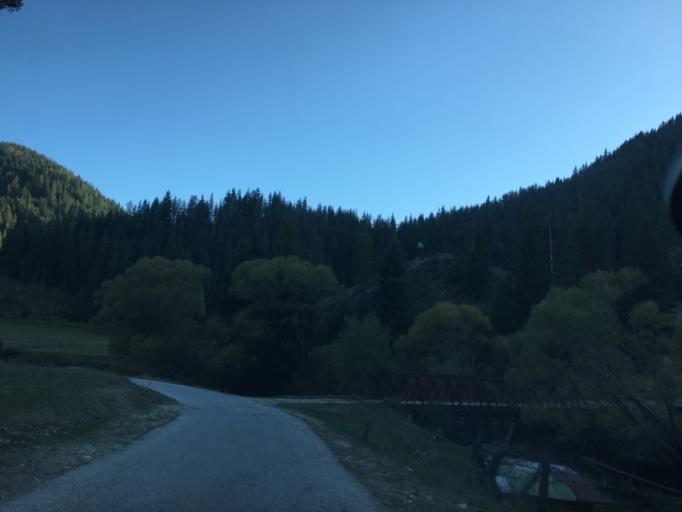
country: BG
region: Smolyan
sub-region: Obshtina Borino
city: Borino
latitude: 41.5856
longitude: 24.3910
